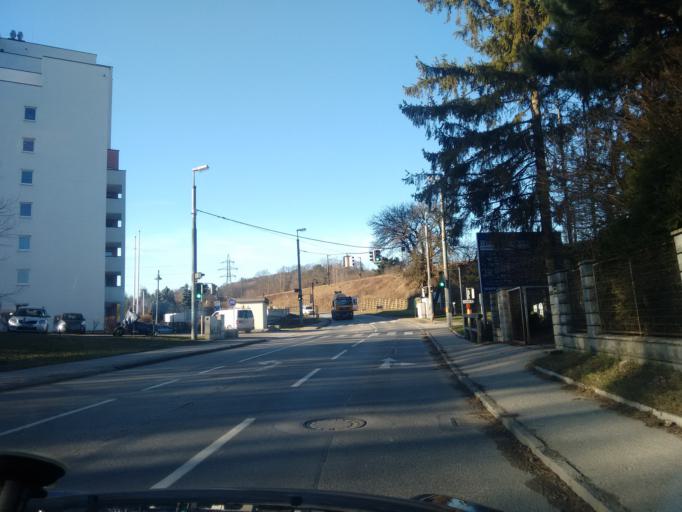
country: AT
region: Lower Austria
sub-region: Politischer Bezirk Wien-Umgebung
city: Pressbaum
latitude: 48.1778
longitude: 16.0576
